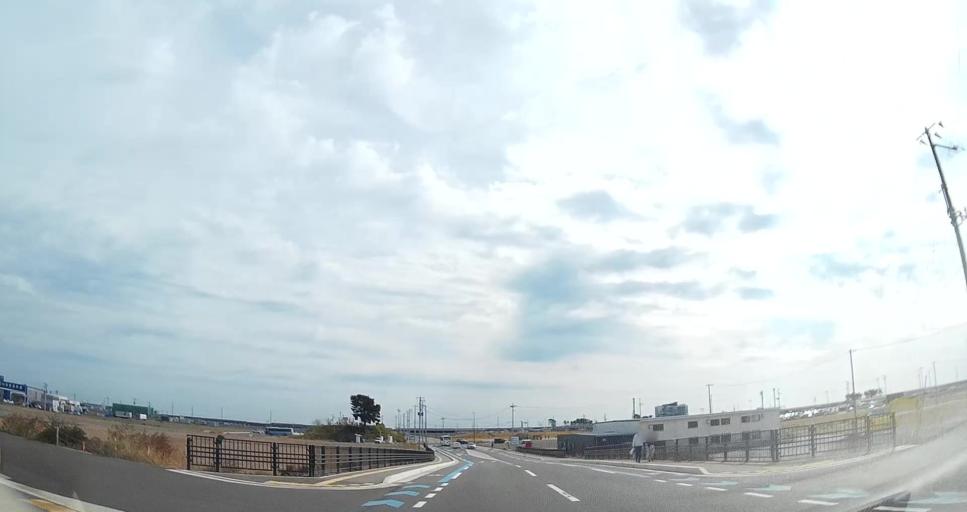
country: JP
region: Miyagi
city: Iwanuma
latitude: 38.1730
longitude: 140.9517
